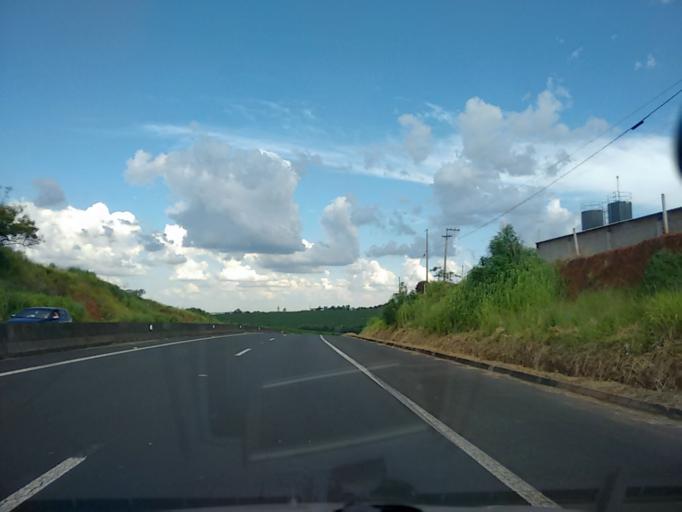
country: BR
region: Sao Paulo
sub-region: Marilia
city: Marilia
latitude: -22.2154
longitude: -49.8428
